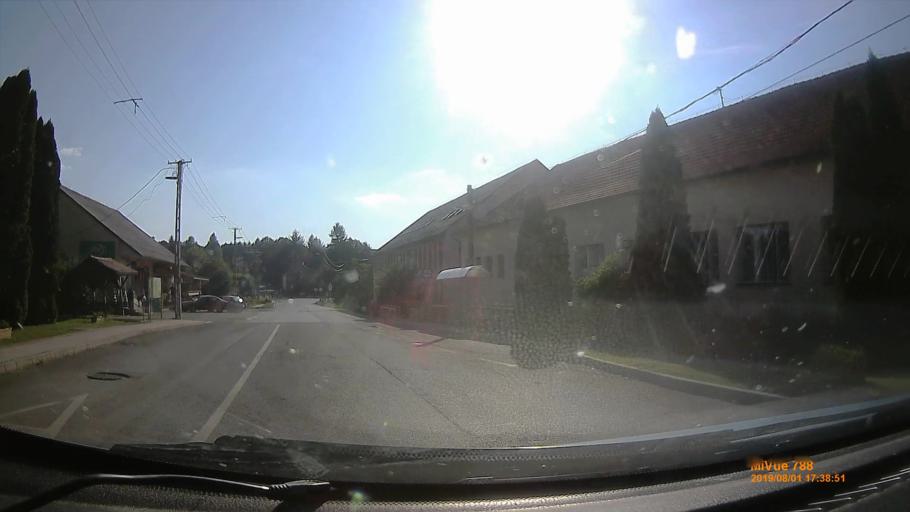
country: HU
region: Baranya
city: Komlo
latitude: 46.1967
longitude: 18.1966
